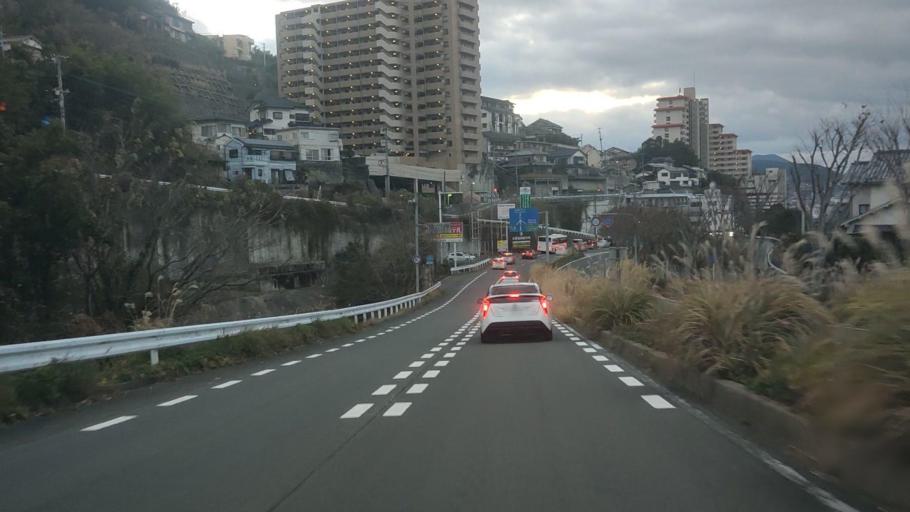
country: JP
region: Nagasaki
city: Nagasaki-shi
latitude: 32.7684
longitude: 129.8912
